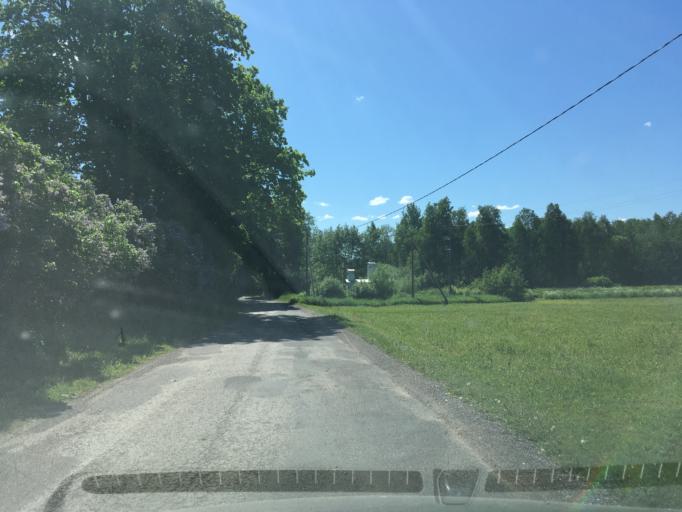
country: EE
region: Harju
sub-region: Rae vald
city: Vaida
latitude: 59.1642
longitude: 25.1244
